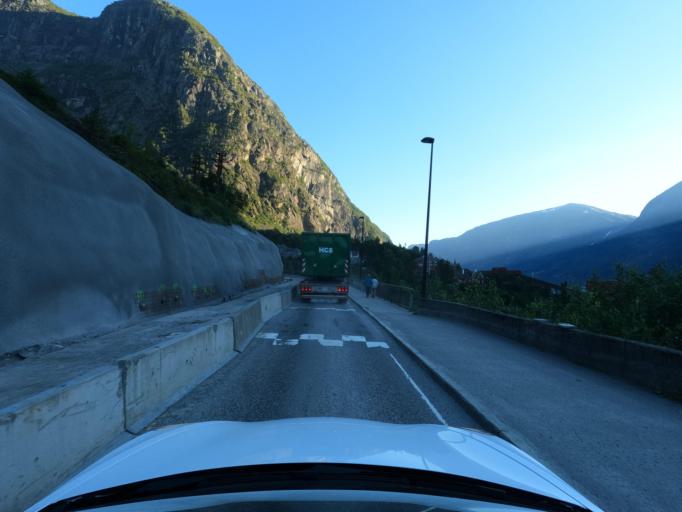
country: NO
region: Hordaland
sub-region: Odda
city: Odda
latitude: 60.1186
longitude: 6.5579
